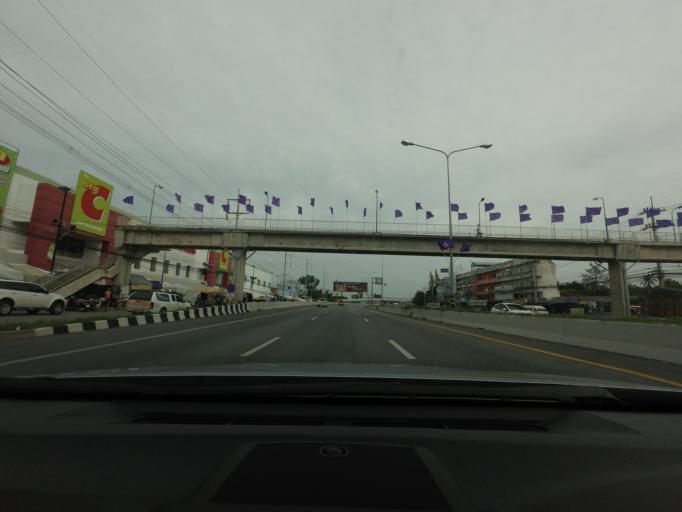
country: TH
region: Phetchaburi
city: Phetchaburi
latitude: 13.0791
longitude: 99.9473
